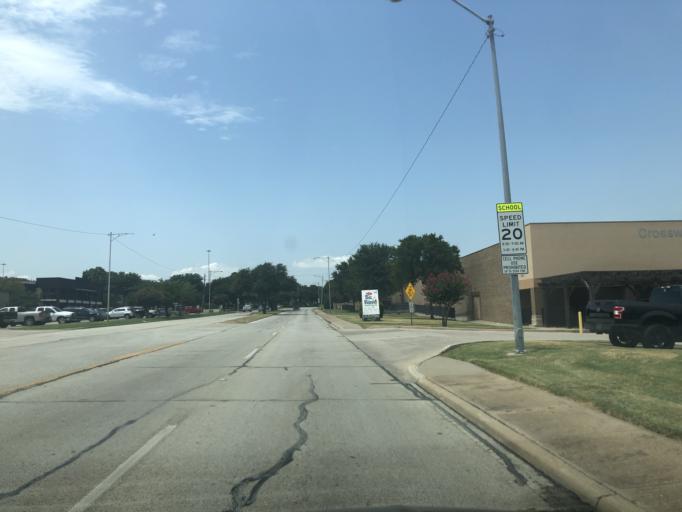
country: US
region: Texas
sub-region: Dallas County
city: Grand Prairie
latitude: 32.7557
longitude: -97.0185
